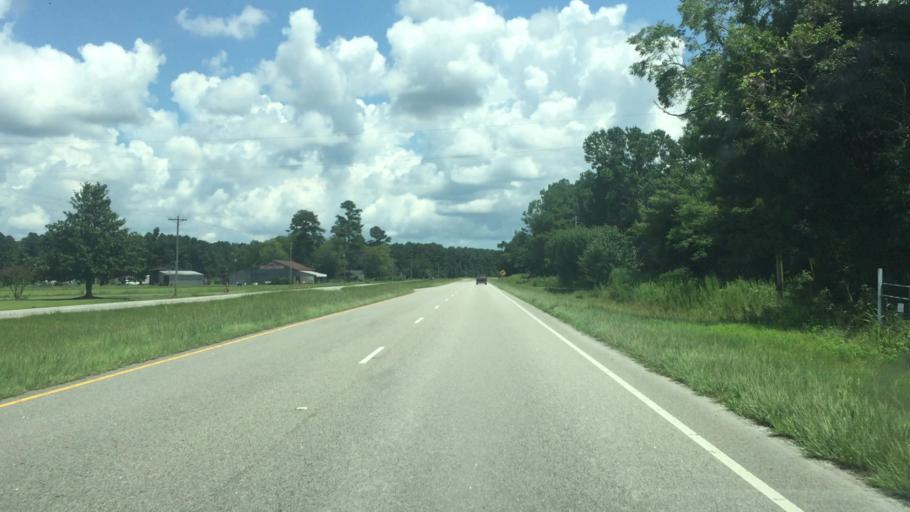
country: US
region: South Carolina
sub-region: Horry County
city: Loris
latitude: 34.0092
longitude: -78.7692
